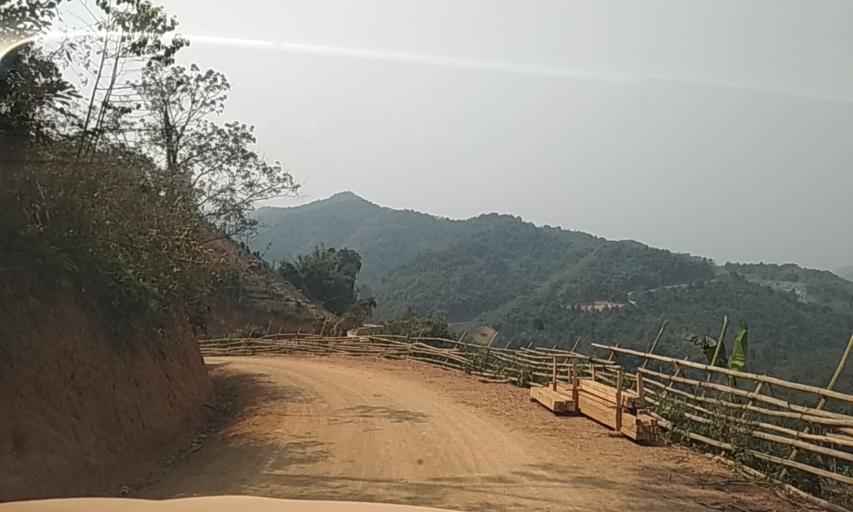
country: LA
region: Phongsali
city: Phongsali
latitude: 21.4754
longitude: 102.4348
